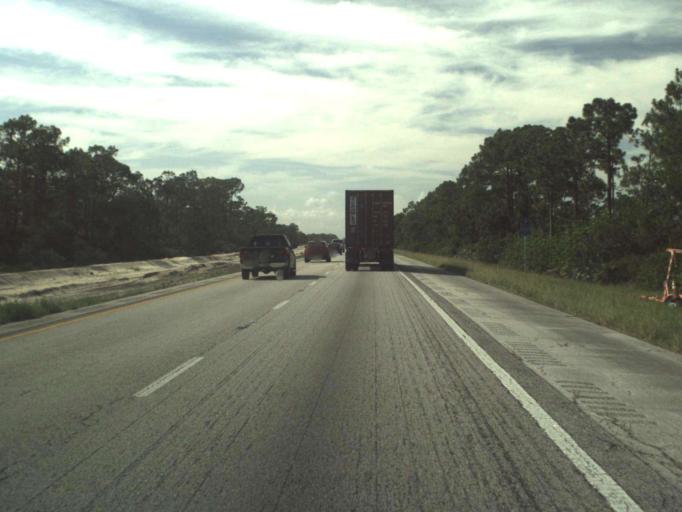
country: US
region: Florida
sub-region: Indian River County
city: West Vero Corridor
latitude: 27.6561
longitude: -80.5257
